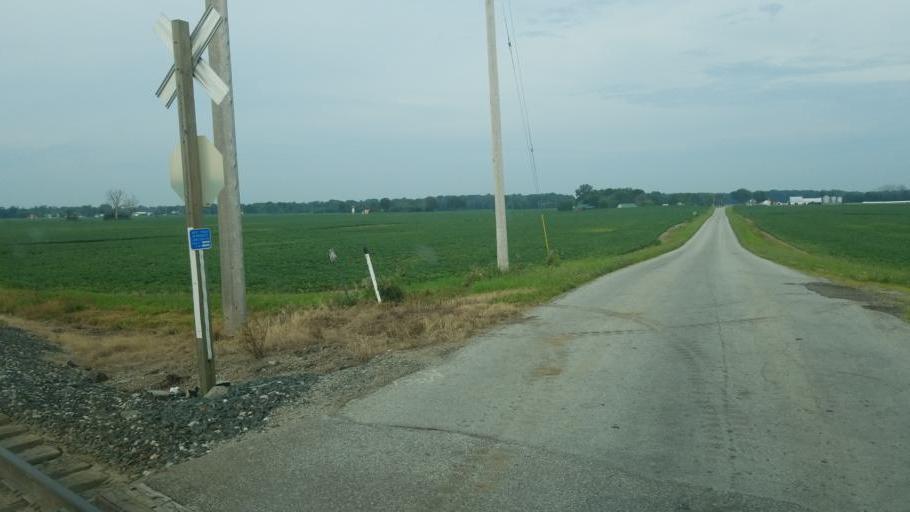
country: US
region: Ohio
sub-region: Morrow County
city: Cardington
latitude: 40.5164
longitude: -82.8873
